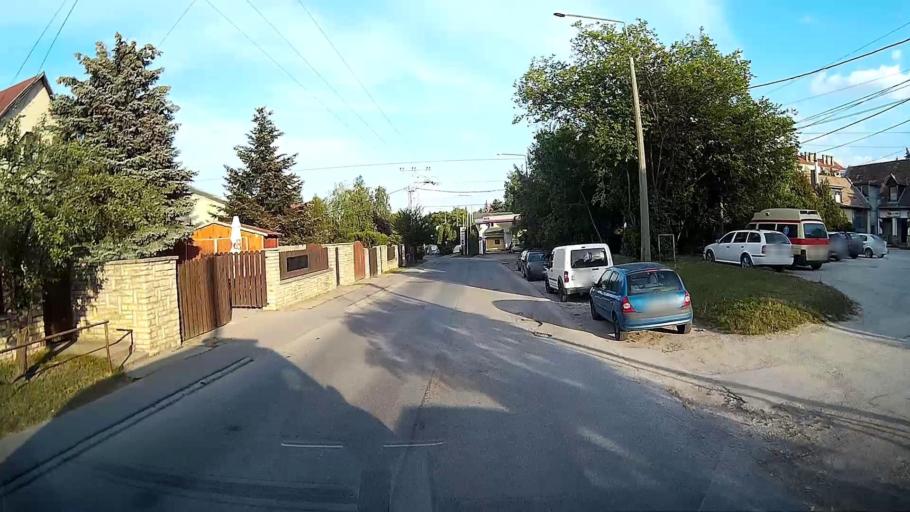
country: HU
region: Pest
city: Szentendre
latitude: 47.6758
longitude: 19.0675
